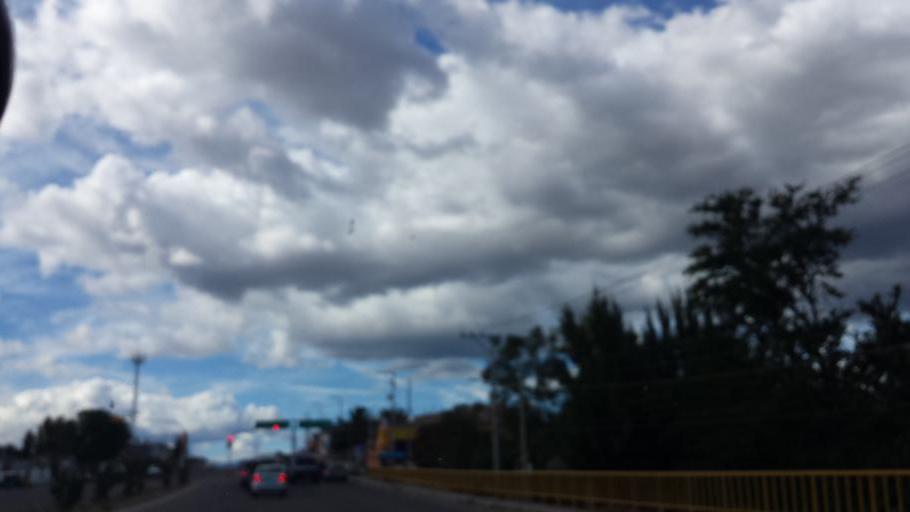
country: MX
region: Oaxaca
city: Tlacolula de Matamoros
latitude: 16.9565
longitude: -96.4721
